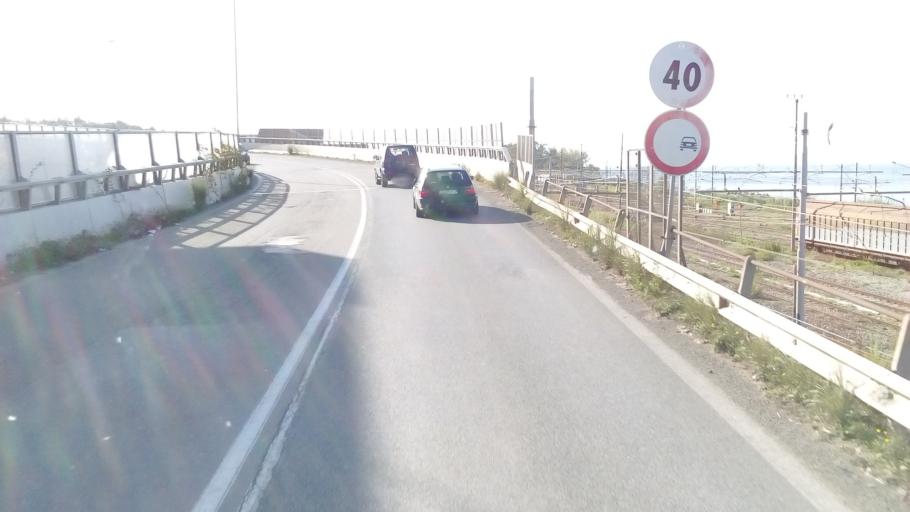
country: IT
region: Calabria
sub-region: Provincia di Reggio Calabria
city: Campo Calabro
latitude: 38.2078
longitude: 15.6354
